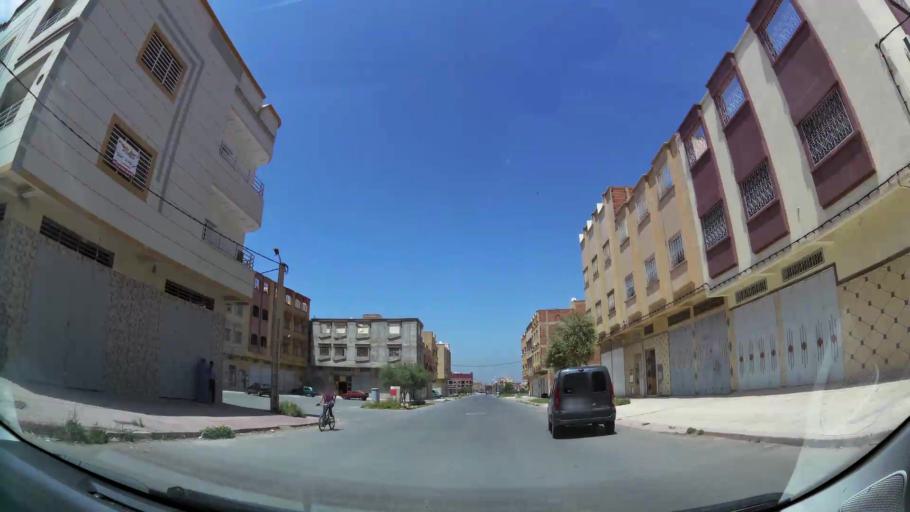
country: MA
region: Oriental
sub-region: Oujda-Angad
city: Oujda
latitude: 34.6928
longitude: -1.8881
